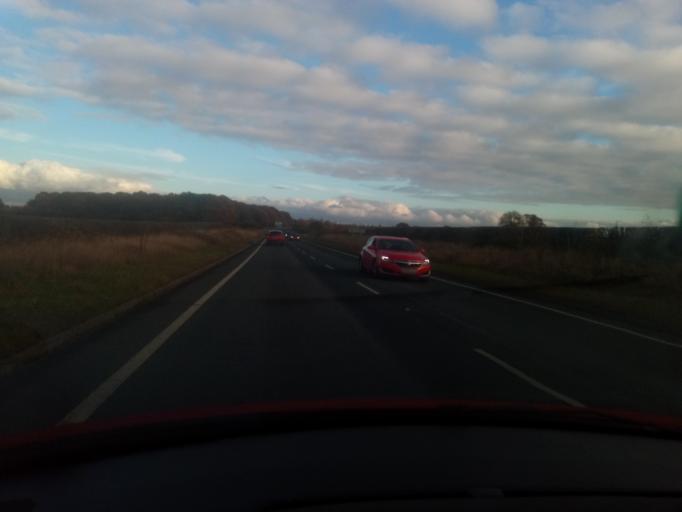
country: GB
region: England
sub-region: City and Borough of Leeds
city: Wetherby
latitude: 53.9451
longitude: -1.3840
